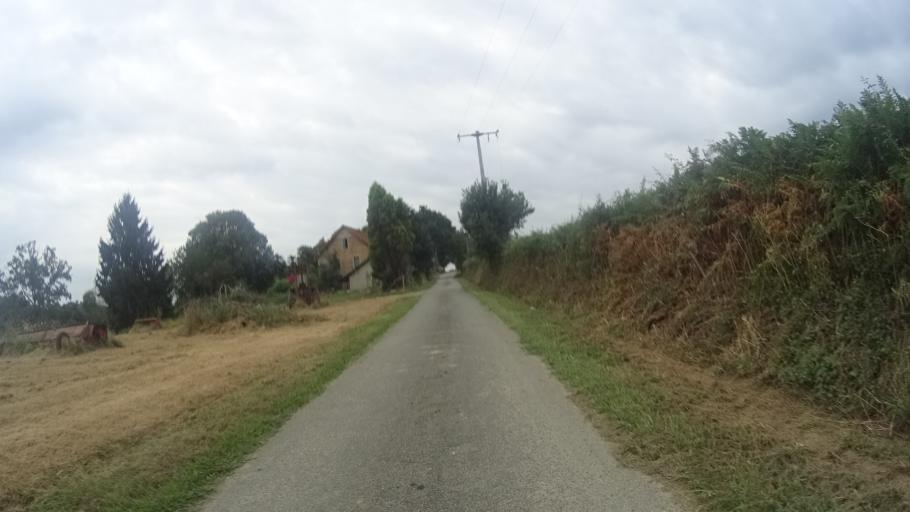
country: FR
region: Aquitaine
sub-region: Departement des Pyrenees-Atlantiques
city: Mont
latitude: 43.4955
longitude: -0.6898
